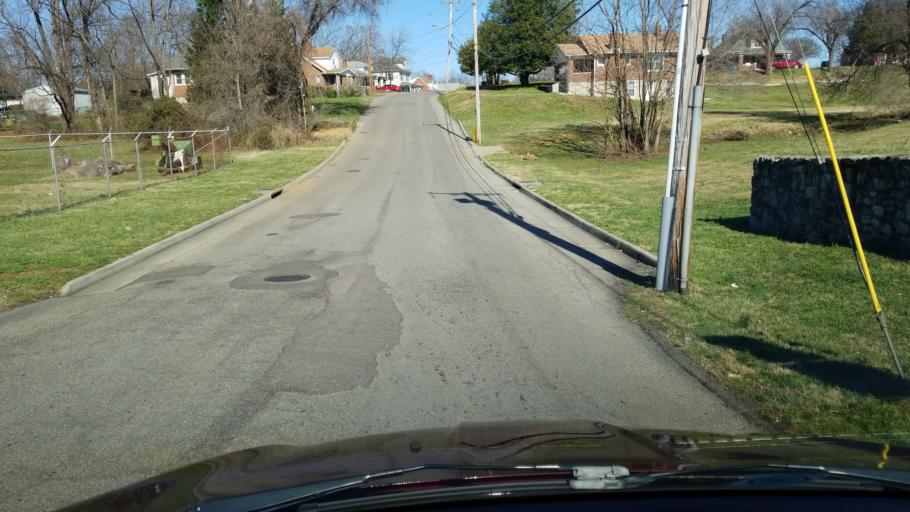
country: US
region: Virginia
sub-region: City of Roanoke
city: Roanoke
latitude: 37.2987
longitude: -79.9394
